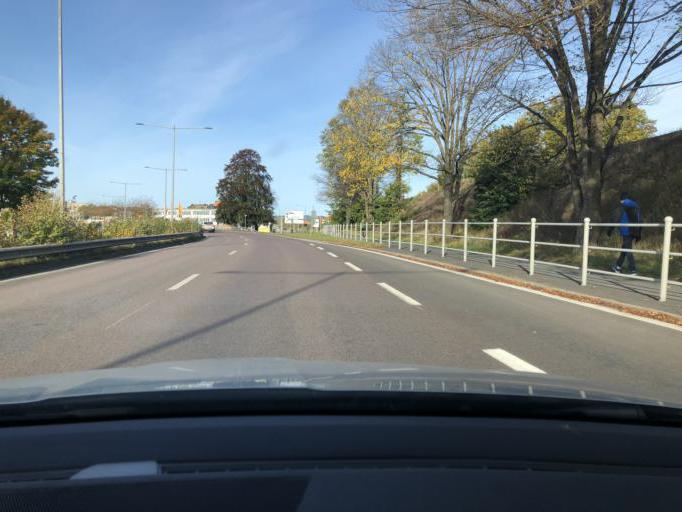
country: SE
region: Joenkoeping
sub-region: Jonkopings Kommun
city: Jonkoping
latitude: 57.7782
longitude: 14.1958
